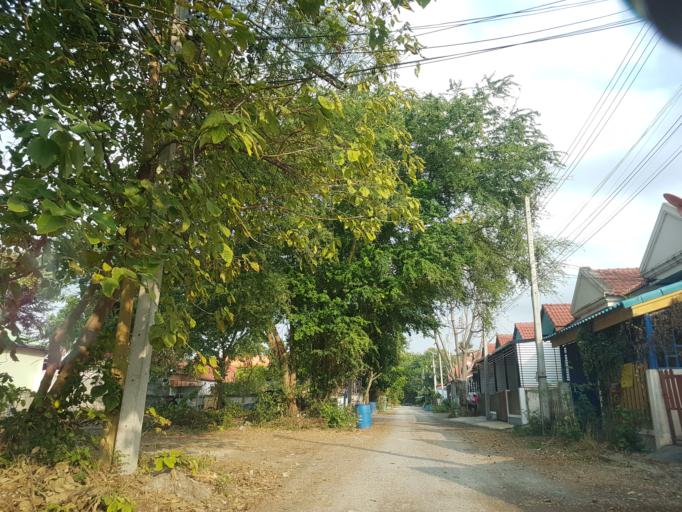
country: TH
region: Lop Buri
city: Lop Buri
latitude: 14.7692
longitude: 100.6967
